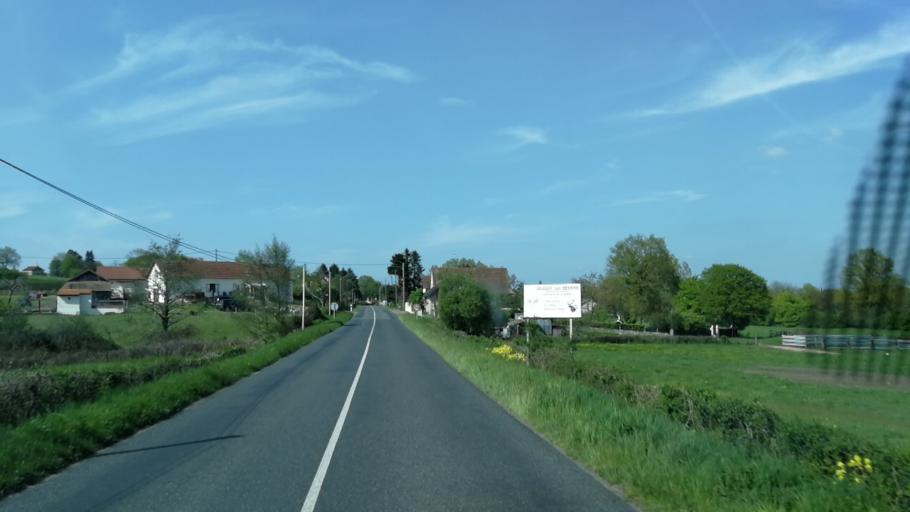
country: FR
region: Auvergne
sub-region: Departement de l'Allier
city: Saint-Gerand-le-Puy
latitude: 46.3693
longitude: 3.5807
